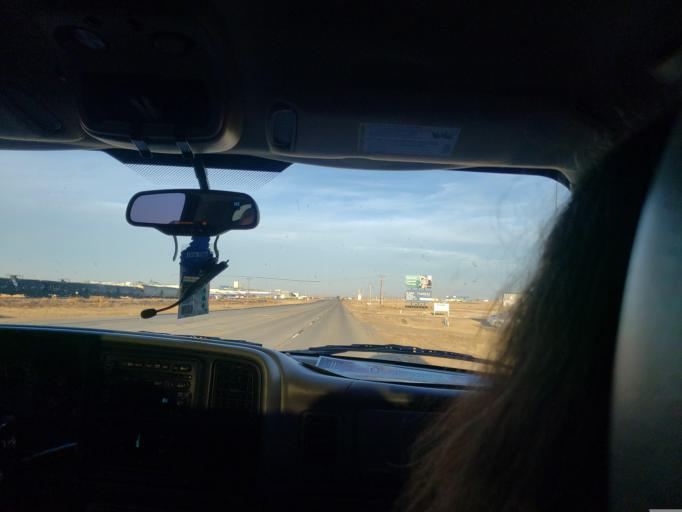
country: US
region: Oklahoma
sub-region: Texas County
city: Guymon
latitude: 36.7026
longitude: -101.4497
